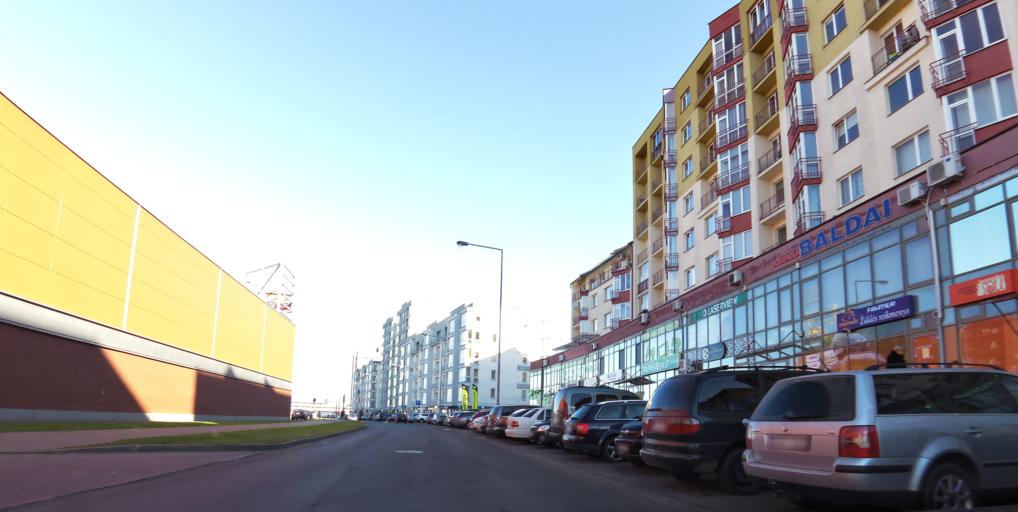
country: LT
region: Vilnius County
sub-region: Vilnius
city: Vilnius
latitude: 54.7089
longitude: 25.3026
